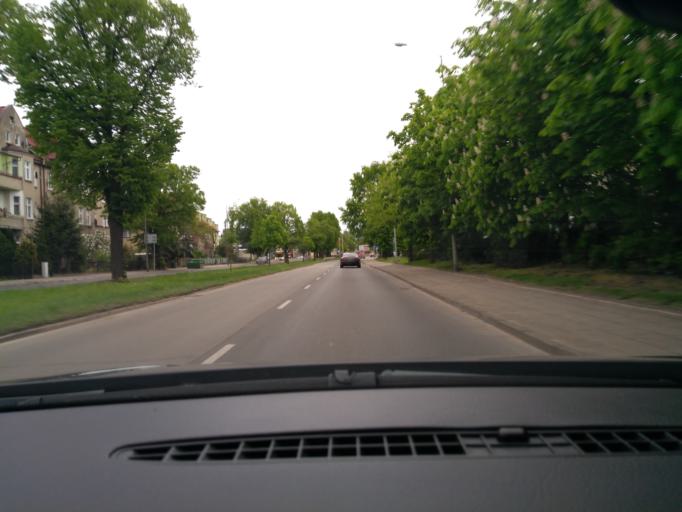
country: PL
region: West Pomeranian Voivodeship
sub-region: Szczecin
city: Szczecin
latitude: 53.3849
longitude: 14.6313
